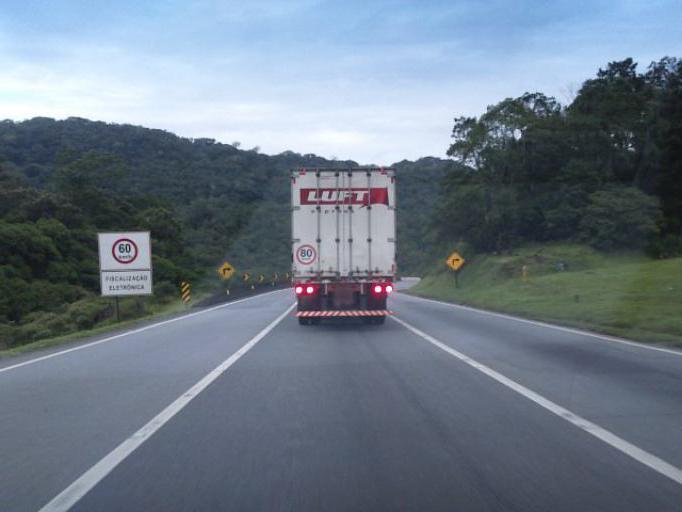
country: BR
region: Parana
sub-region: Guaratuba
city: Guaratuba
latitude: -25.8661
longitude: -48.9461
